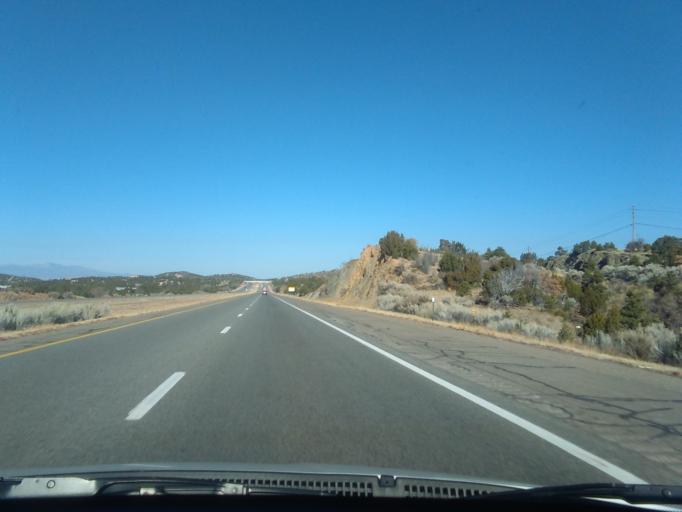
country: US
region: New Mexico
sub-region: Santa Fe County
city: Eldorado at Santa Fe
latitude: 35.5899
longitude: -105.9028
